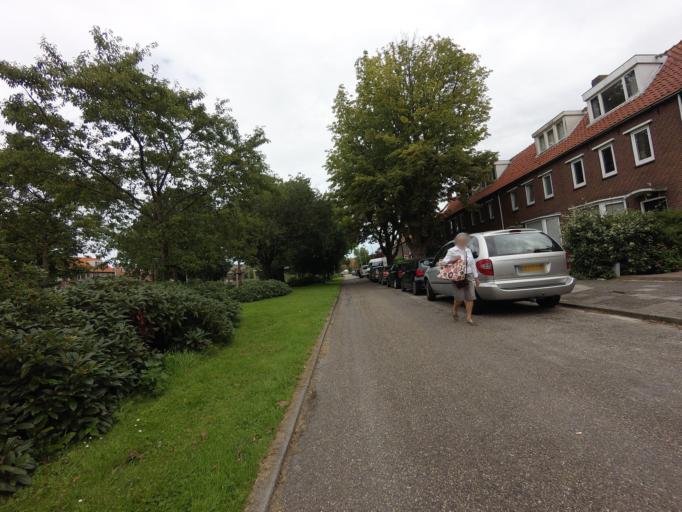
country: NL
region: North Holland
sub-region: Gemeente Uithoorn
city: Uithoorn
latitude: 52.2333
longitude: 4.8307
